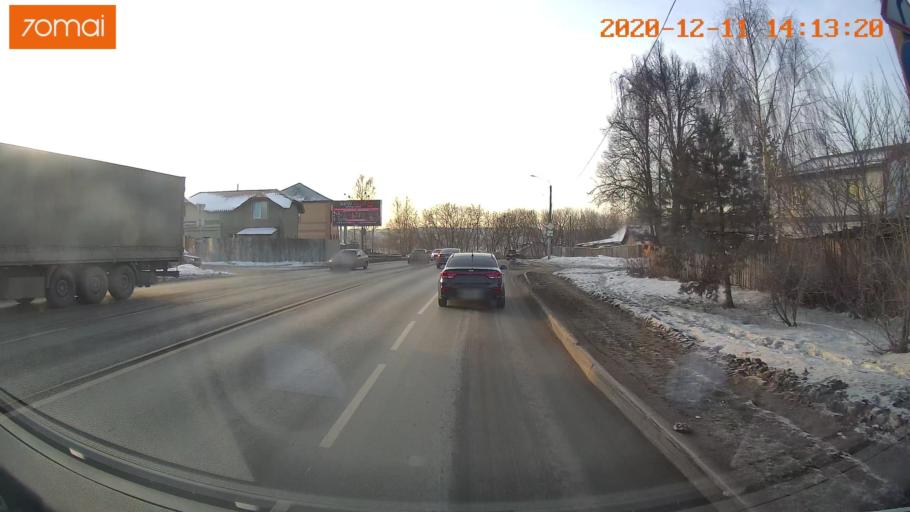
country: RU
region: Kostroma
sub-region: Kostromskoy Rayon
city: Kostroma
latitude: 57.7459
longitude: 40.9597
